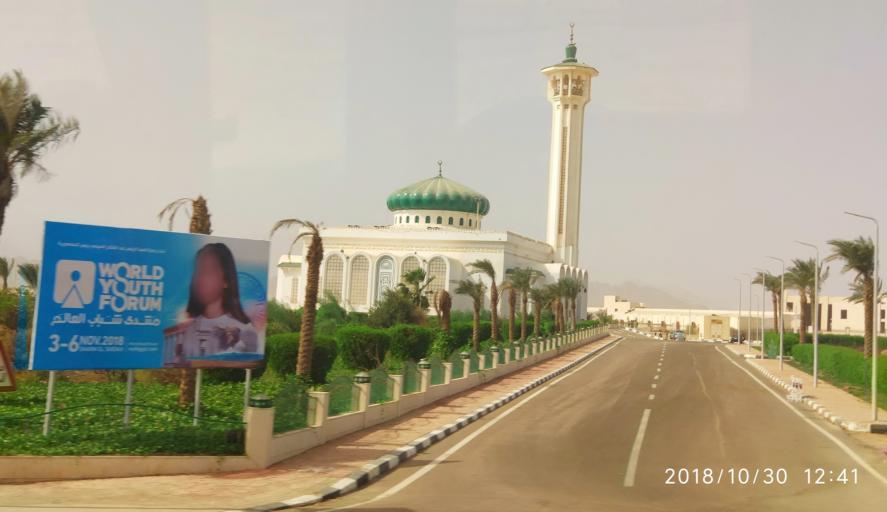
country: EG
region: South Sinai
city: Sharm el-Sheikh
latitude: 27.9284
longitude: 34.3471
